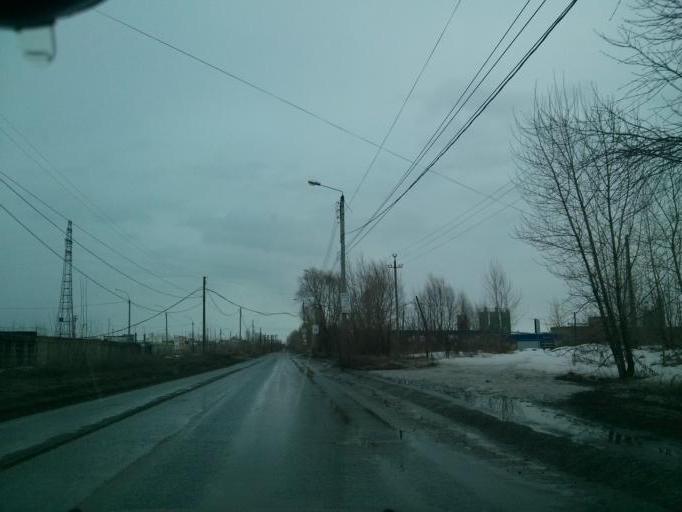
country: RU
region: Nizjnij Novgorod
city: Afonino
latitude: 56.2950
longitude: 44.1089
